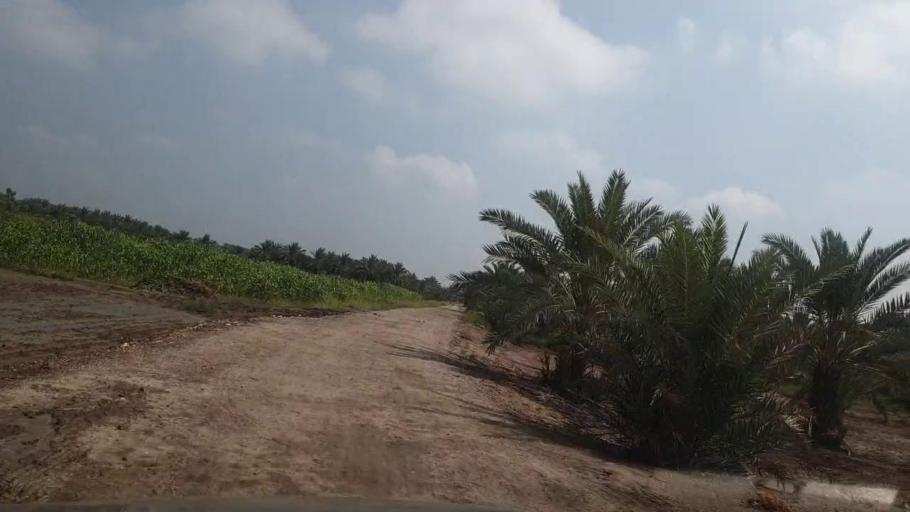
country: PK
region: Sindh
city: Pir jo Goth
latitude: 27.6015
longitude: 68.6946
